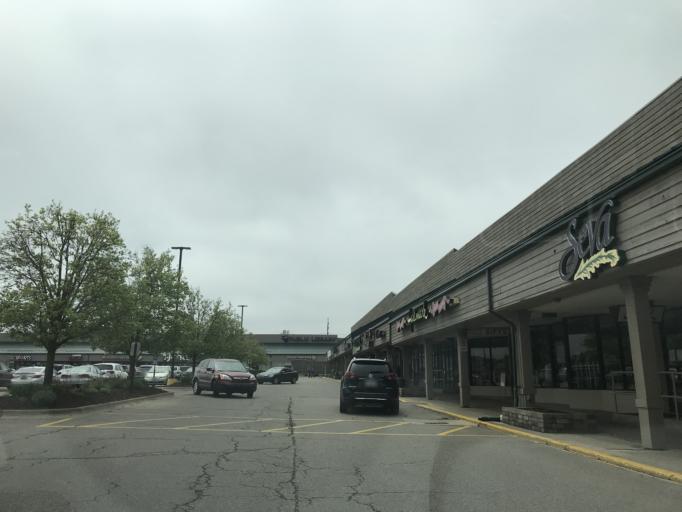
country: US
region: Michigan
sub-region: Washtenaw County
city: Ann Arbor
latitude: 42.2798
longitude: -83.7825
